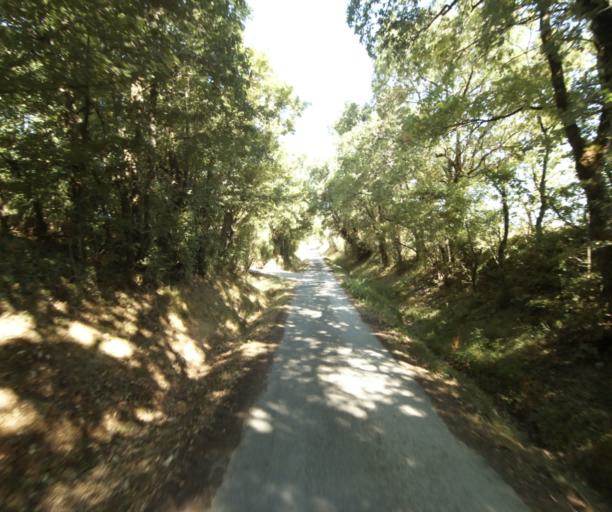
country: FR
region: Midi-Pyrenees
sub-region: Departement de la Haute-Garonne
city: Revel
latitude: 43.4481
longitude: 2.0210
